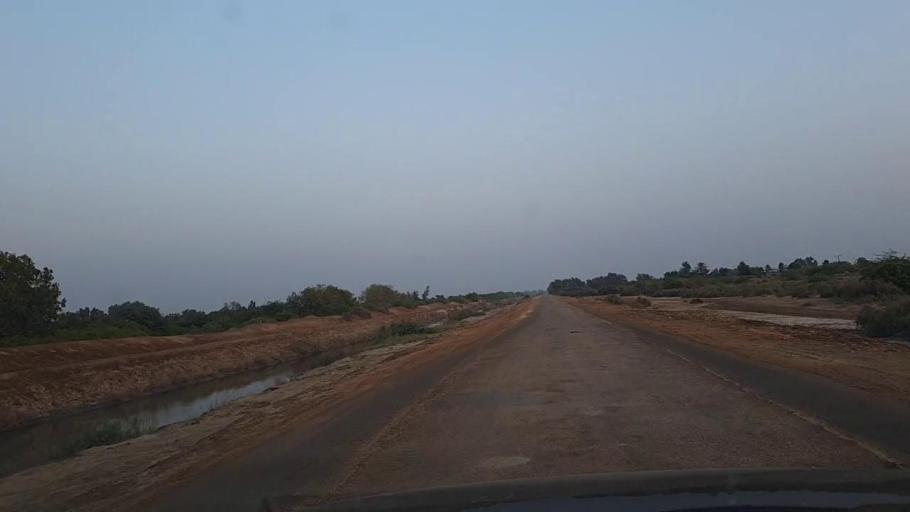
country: PK
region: Sindh
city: Mirpur Sakro
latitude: 24.6325
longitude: 67.6238
